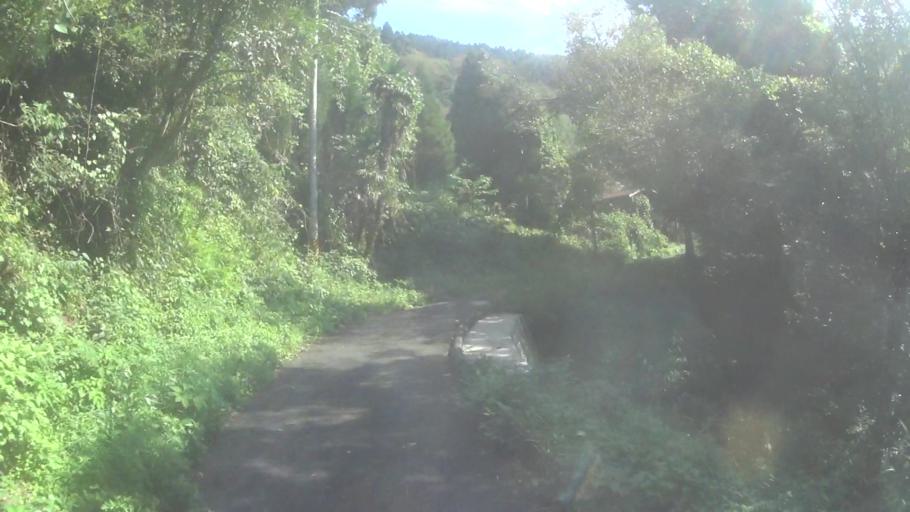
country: JP
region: Kyoto
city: Miyazu
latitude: 35.7157
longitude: 135.1658
